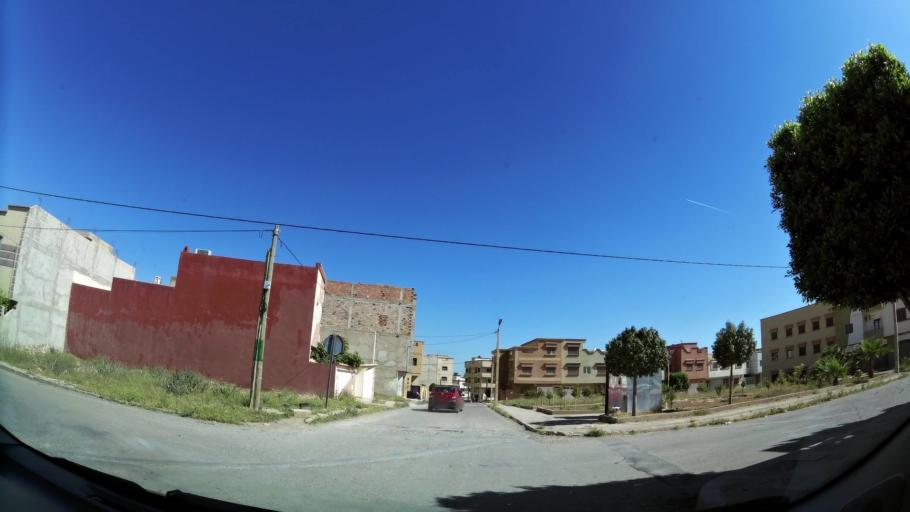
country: MA
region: Oriental
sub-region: Oujda-Angad
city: Oujda
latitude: 34.6514
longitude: -1.8856
